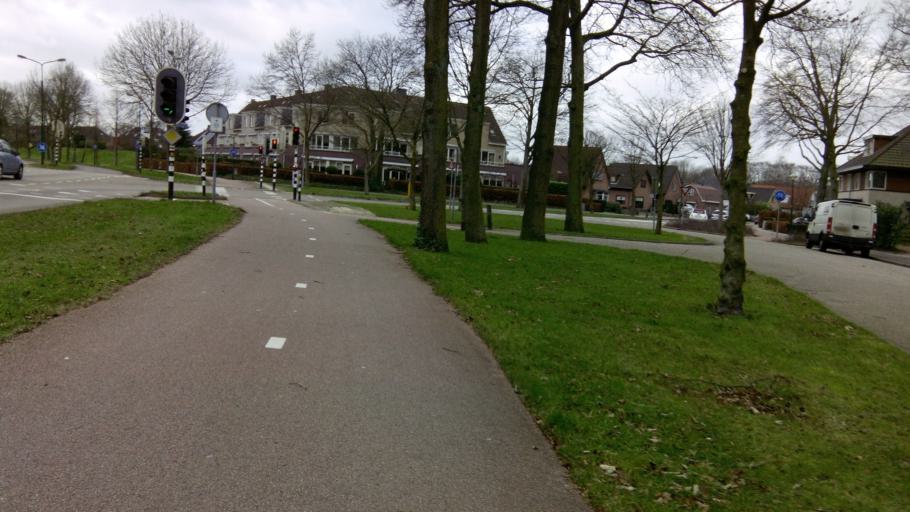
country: NL
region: Utrecht
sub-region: Gemeente Soest
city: Soest
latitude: 52.1658
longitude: 5.3006
